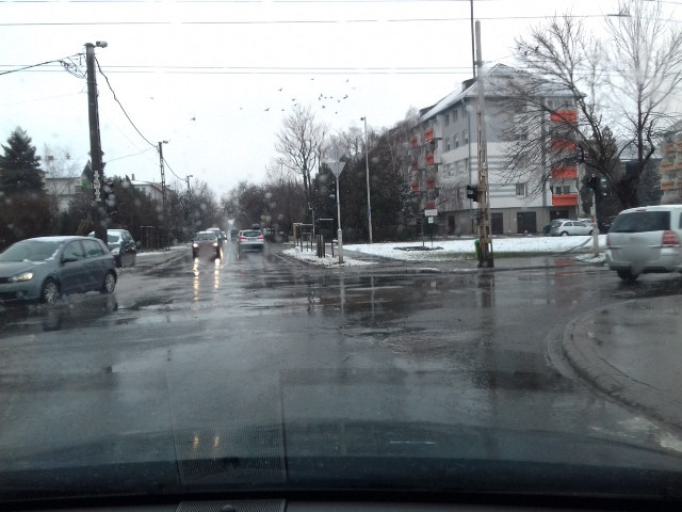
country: HU
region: Budapest
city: Budapest XIV. keruelet
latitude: 47.5173
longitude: 19.1308
